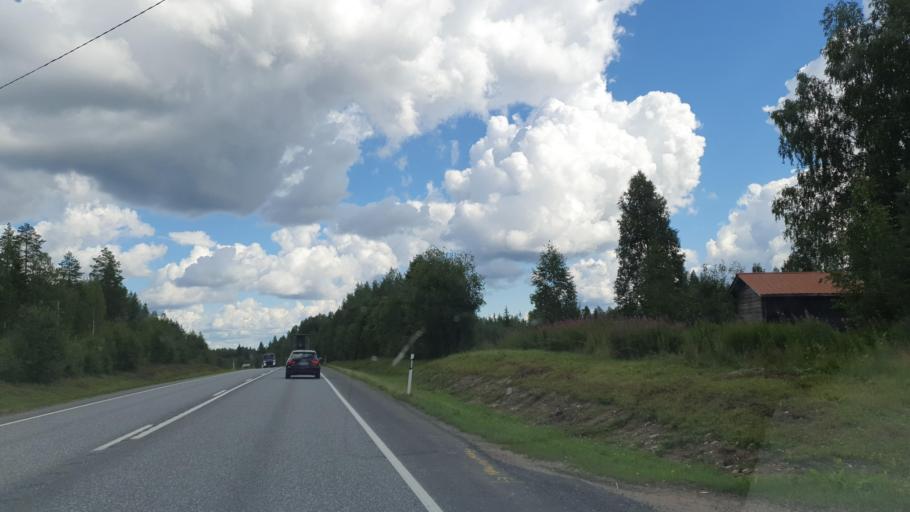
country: FI
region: Kainuu
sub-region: Kajaani
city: Kajaani
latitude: 64.1810
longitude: 27.5859
